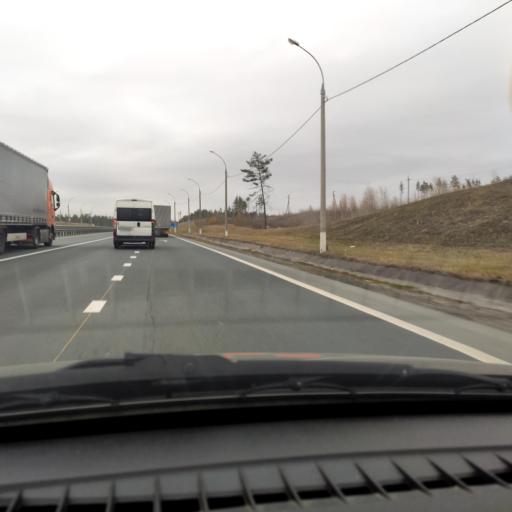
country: RU
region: Samara
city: Zhigulevsk
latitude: 53.4997
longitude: 49.5413
